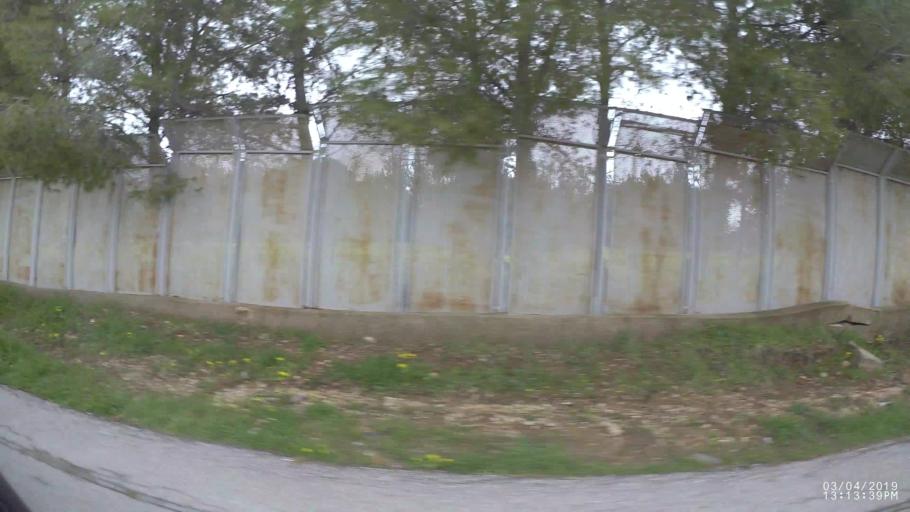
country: JO
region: Amman
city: Wadi as Sir
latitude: 31.9598
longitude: 35.8229
